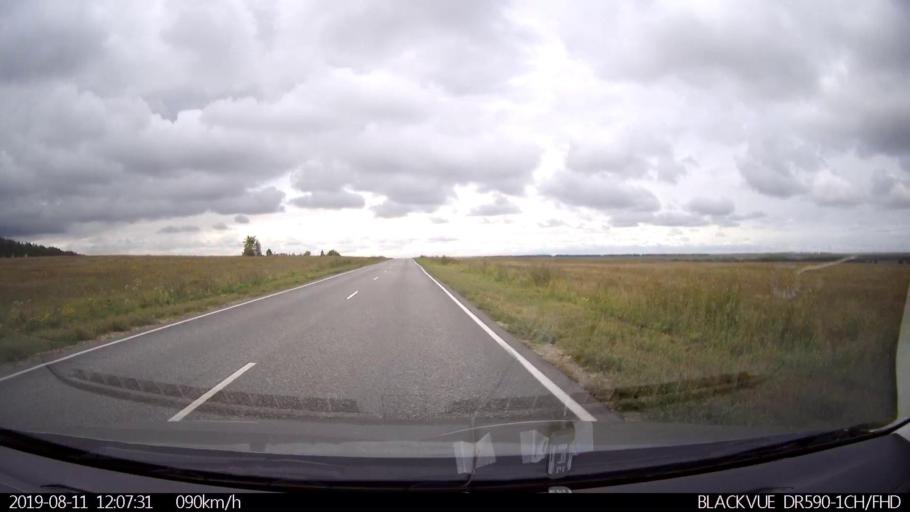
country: RU
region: Ulyanovsk
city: Silikatnyy
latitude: 53.9966
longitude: 48.0930
